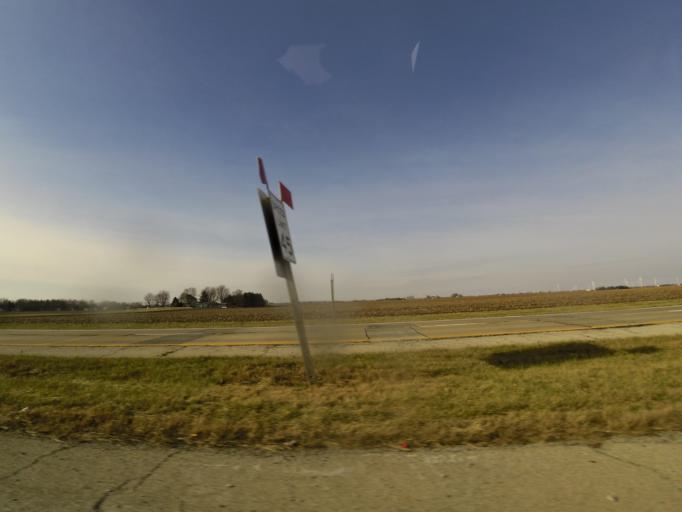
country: US
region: Illinois
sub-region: Macon County
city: Forsyth
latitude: 39.9388
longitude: -88.9555
